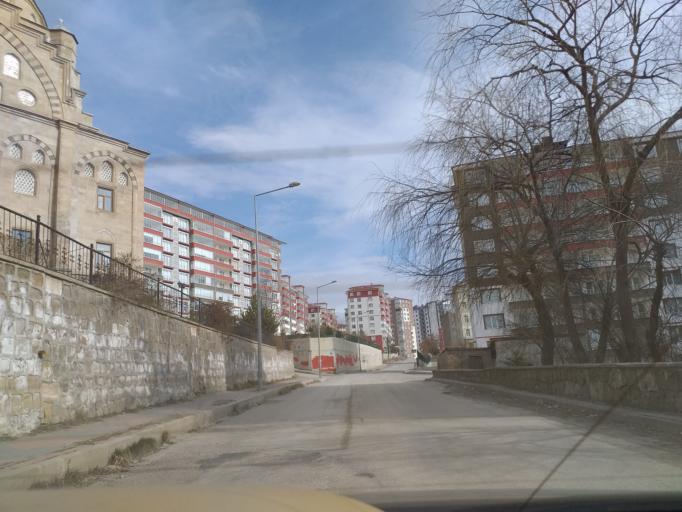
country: TR
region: Yozgat
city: Yozgat
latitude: 39.8300
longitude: 34.8197
